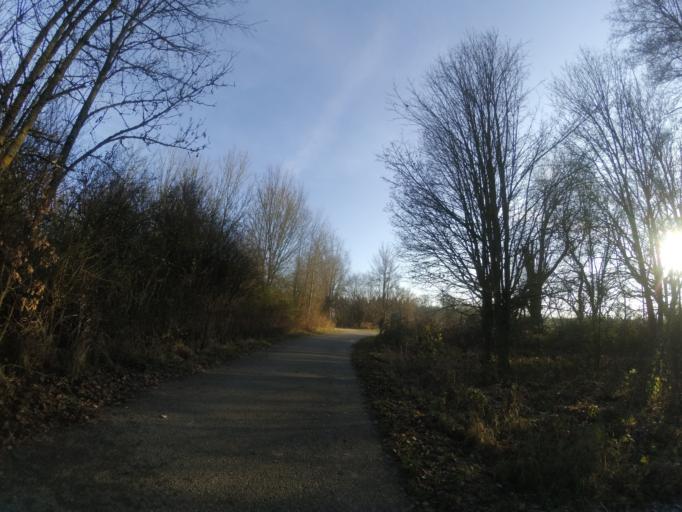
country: DE
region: Baden-Wuerttemberg
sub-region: Tuebingen Region
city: Dornstadt
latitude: 48.4389
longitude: 9.8973
